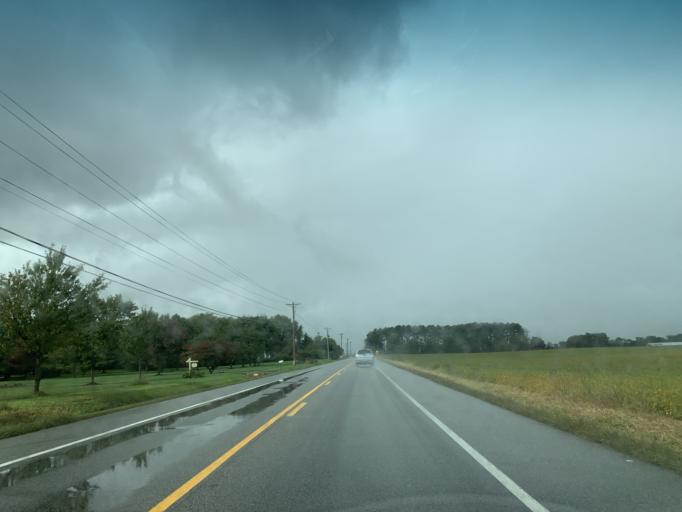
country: US
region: Maryland
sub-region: Queen Anne's County
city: Kingstown
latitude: 39.1987
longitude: -75.8622
